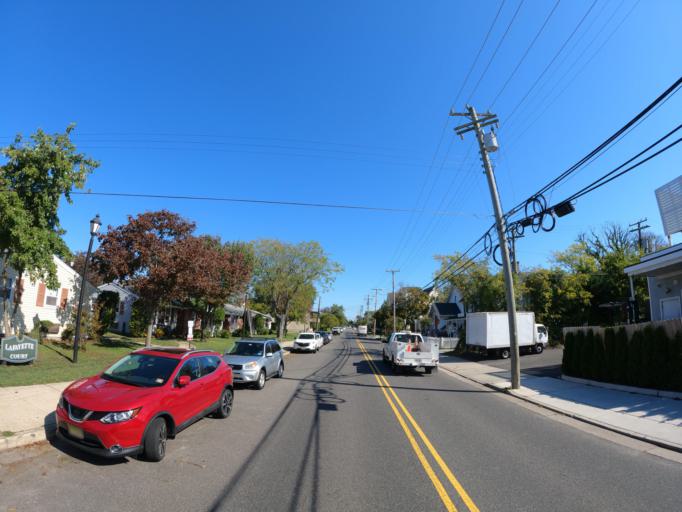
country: US
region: New Jersey
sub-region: Cape May County
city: Cape May
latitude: 38.9351
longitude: -74.9214
